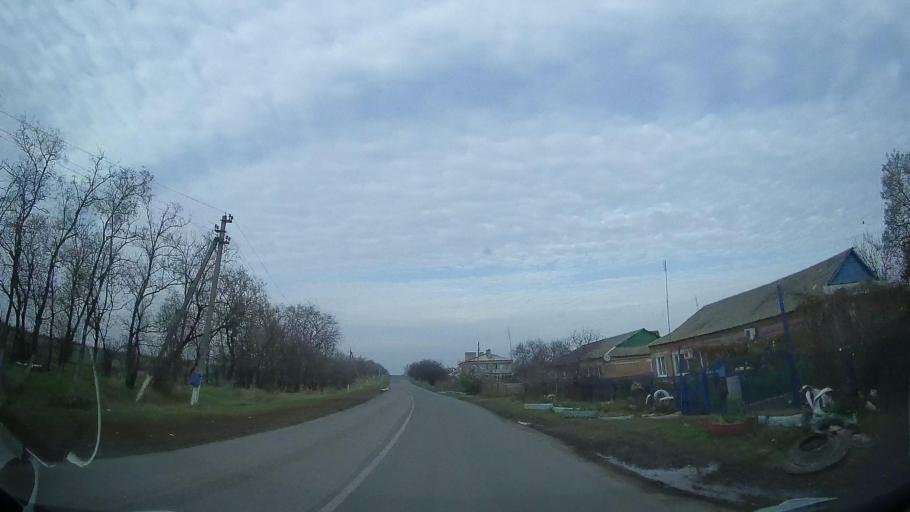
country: RU
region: Rostov
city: Zernograd
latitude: 46.9260
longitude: 40.3662
